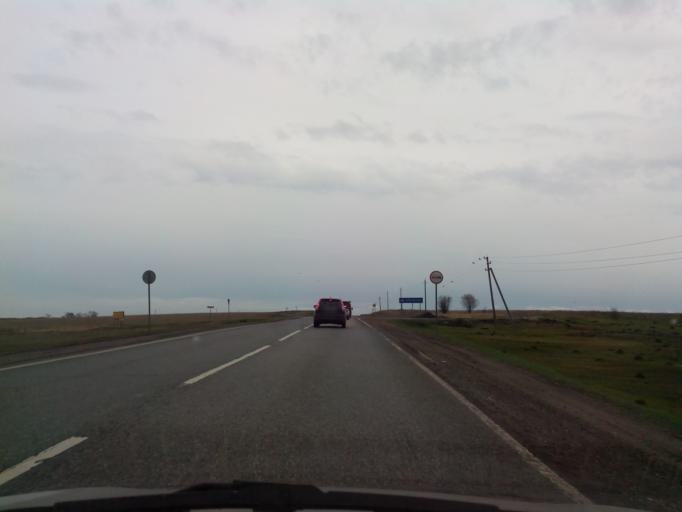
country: RU
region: Moskovskaya
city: Ozherel'ye
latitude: 54.7166
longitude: 38.2833
